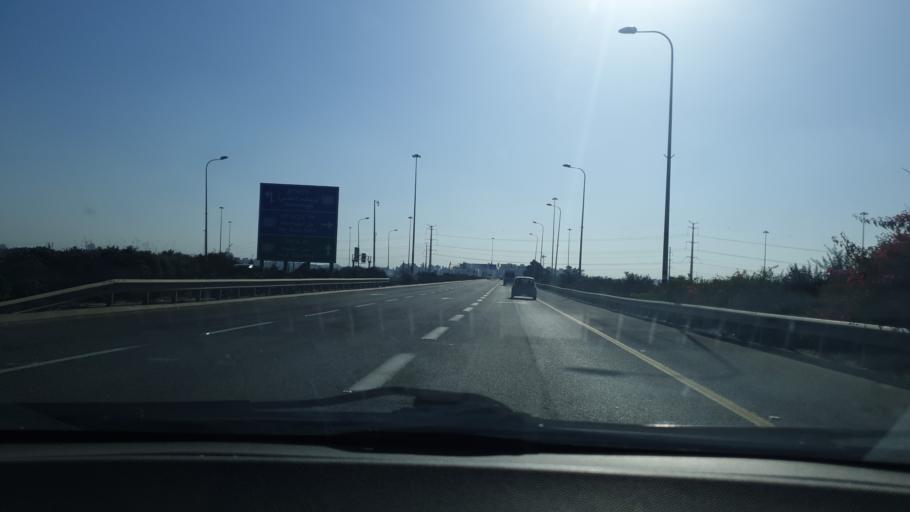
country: IL
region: Central District
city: Ness Ziona
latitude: 31.9425
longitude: 34.8189
